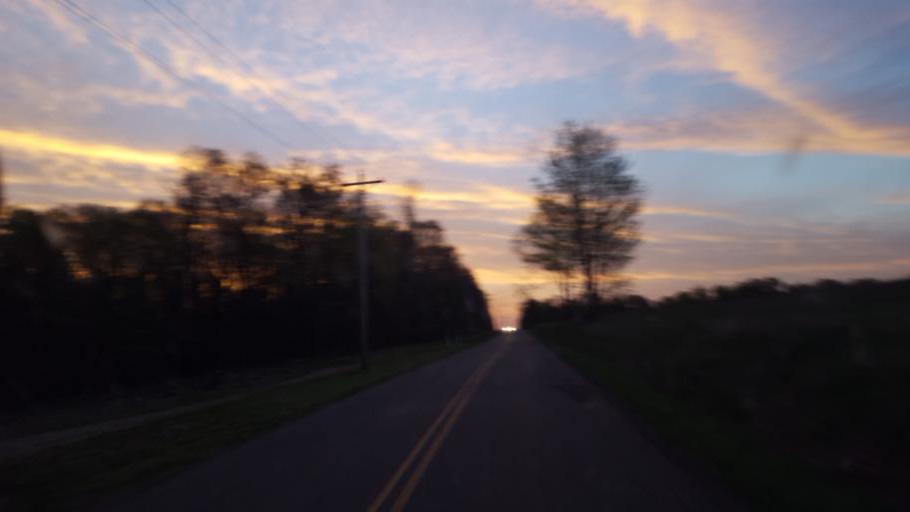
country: US
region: Ohio
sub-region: Knox County
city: Gambier
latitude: 40.4718
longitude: -82.4199
